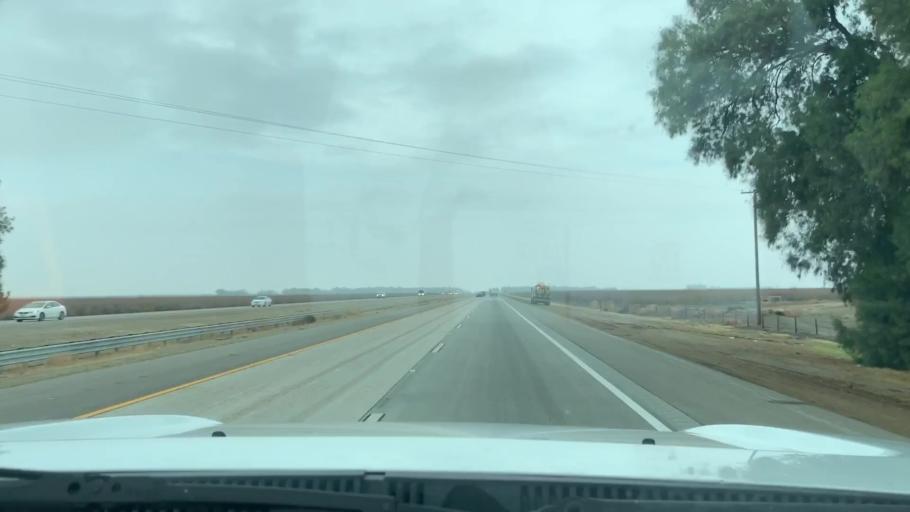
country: US
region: California
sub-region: Kern County
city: Lost Hills
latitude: 35.5768
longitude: -119.6174
